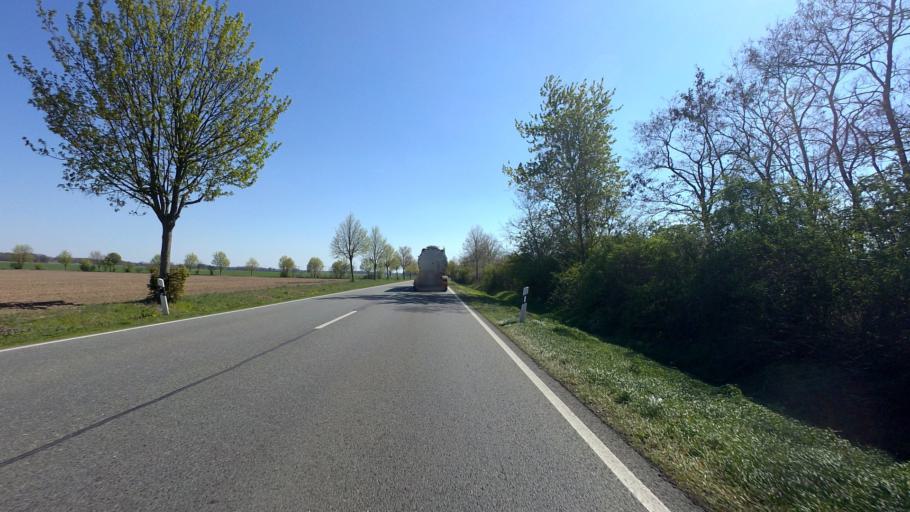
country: DE
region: Saxony-Anhalt
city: Pretzier
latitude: 52.7845
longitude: 11.2328
